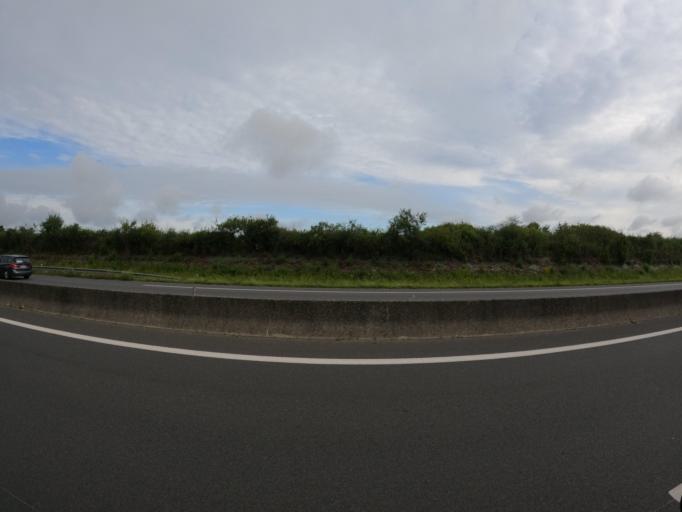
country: FR
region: Centre
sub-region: Departement d'Indre-et-Loire
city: Villandry
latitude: 47.3016
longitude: 0.5382
